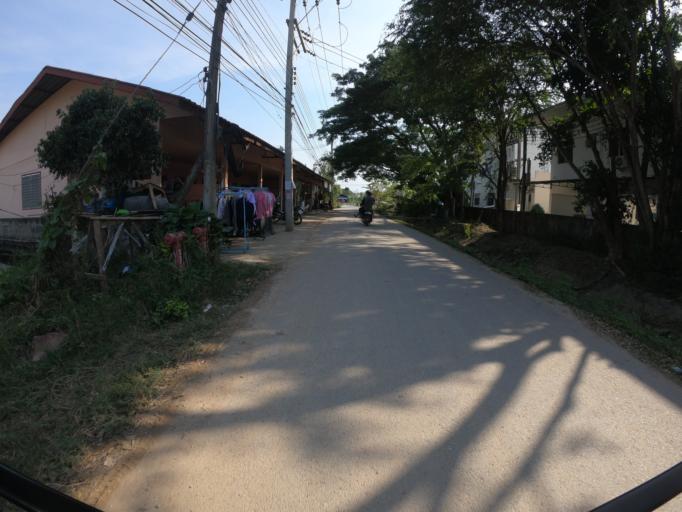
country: TH
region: Chiang Mai
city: Chiang Mai
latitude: 18.8367
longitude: 98.9933
